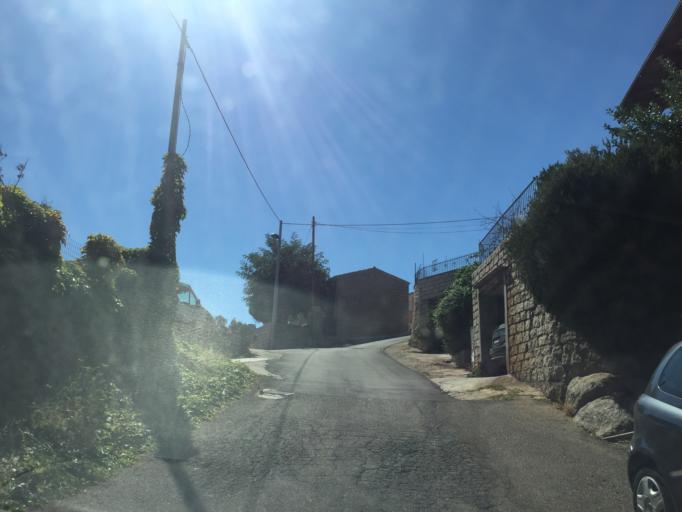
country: IT
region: Sardinia
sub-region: Provincia di Olbia-Tempio
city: Aggius
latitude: 40.9302
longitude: 9.0687
